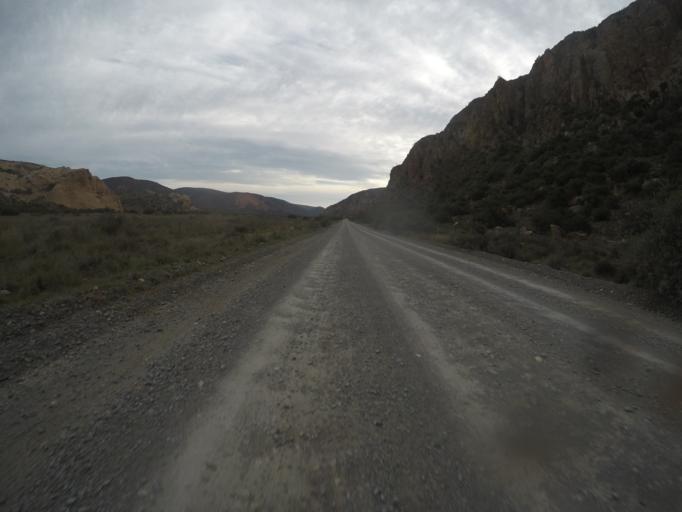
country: ZA
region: Eastern Cape
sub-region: Cacadu District Municipality
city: Willowmore
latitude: -33.5195
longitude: 23.6708
